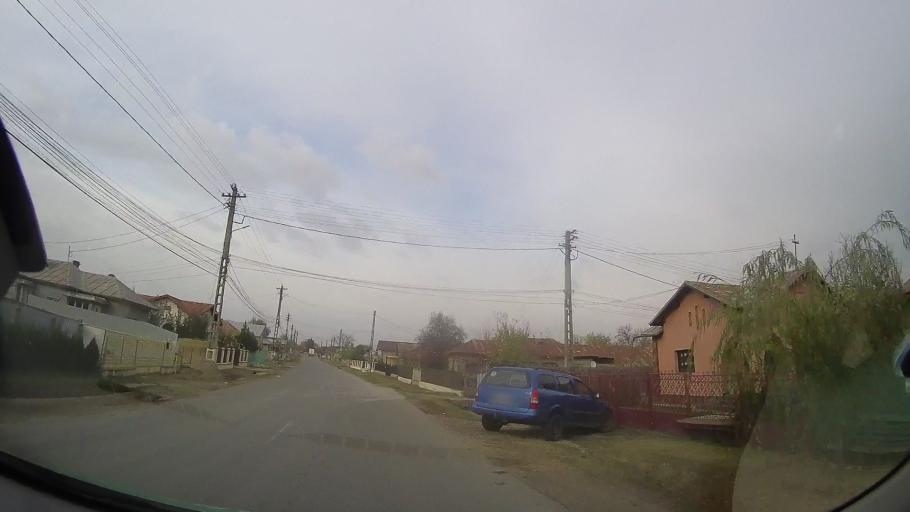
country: RO
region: Prahova
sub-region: Comuna Gorgota
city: Potigrafu
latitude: 44.7815
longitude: 26.1026
